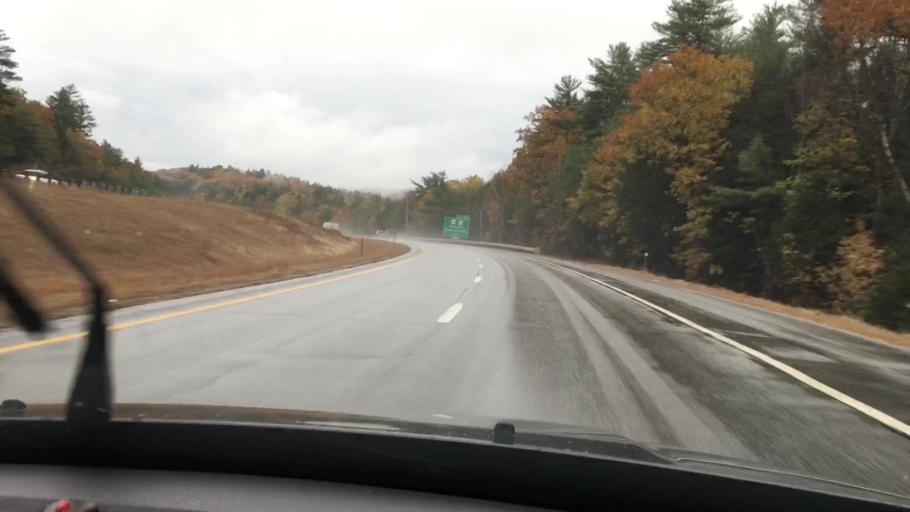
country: US
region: New Hampshire
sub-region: Grafton County
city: Ashland
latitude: 43.6317
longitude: -71.6531
